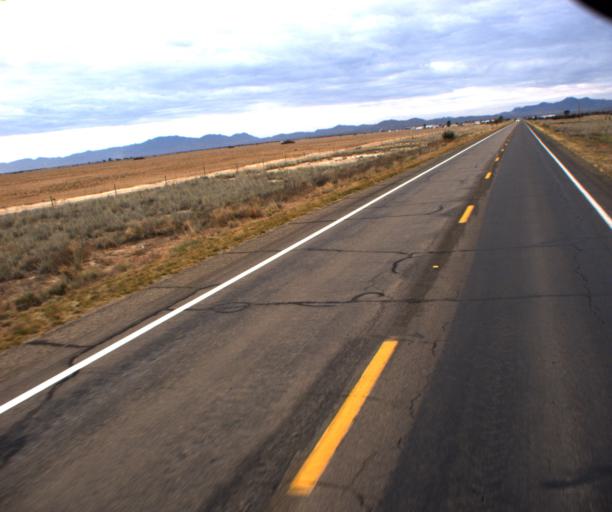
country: US
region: Arizona
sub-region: Cochise County
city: Willcox
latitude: 32.2354
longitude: -109.8508
